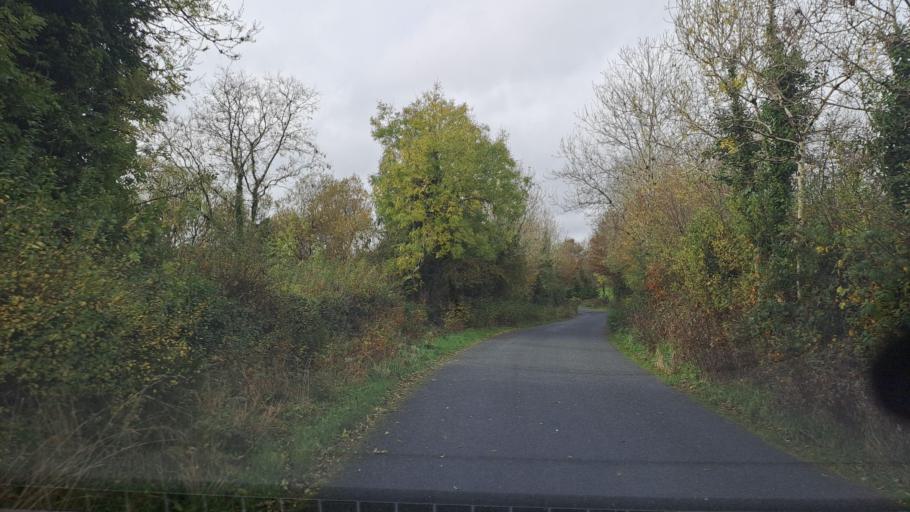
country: IE
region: Ulster
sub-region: An Cabhan
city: Bailieborough
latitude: 54.0487
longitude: -6.9171
